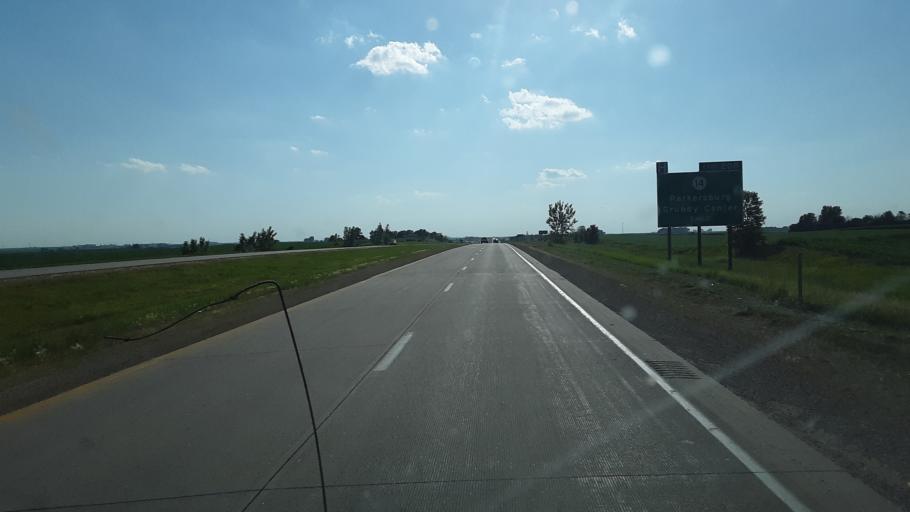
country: US
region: Iowa
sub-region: Grundy County
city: Grundy Center
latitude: 42.4631
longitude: -92.7401
